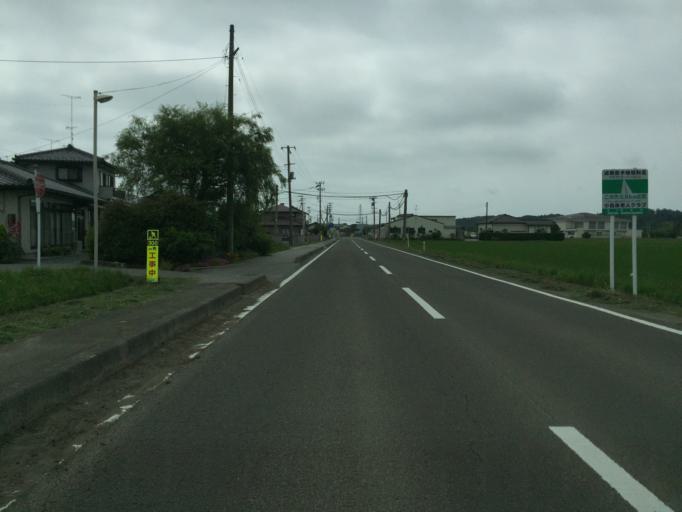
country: JP
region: Fukushima
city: Namie
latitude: 37.6915
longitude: 140.9793
